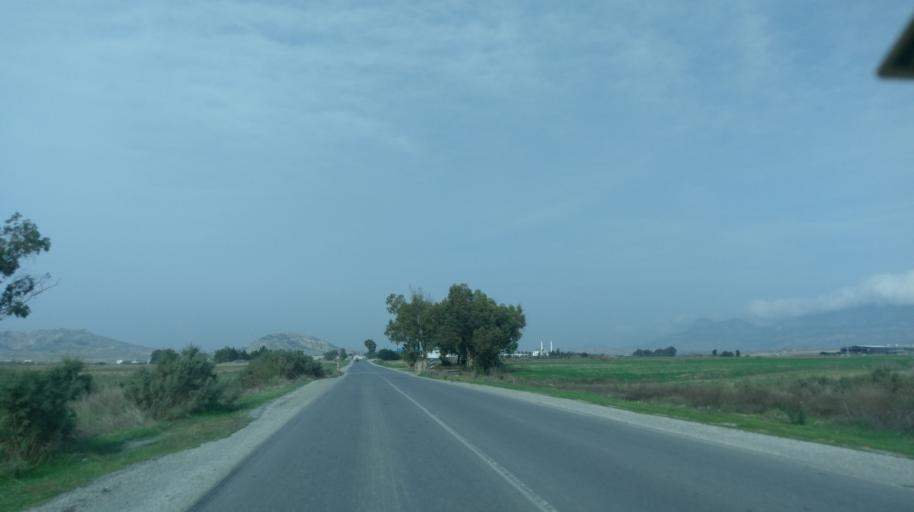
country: CY
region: Lefkosia
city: Mammari
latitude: 35.2225
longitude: 33.1770
